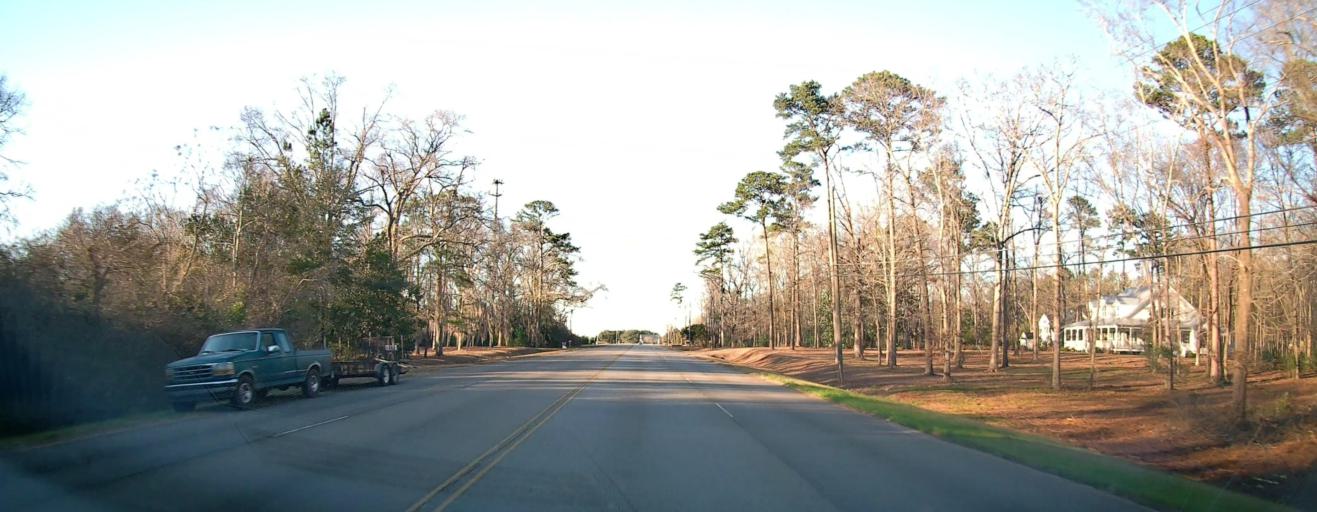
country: US
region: Georgia
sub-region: Dougherty County
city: Albany
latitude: 31.6253
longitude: -84.2292
